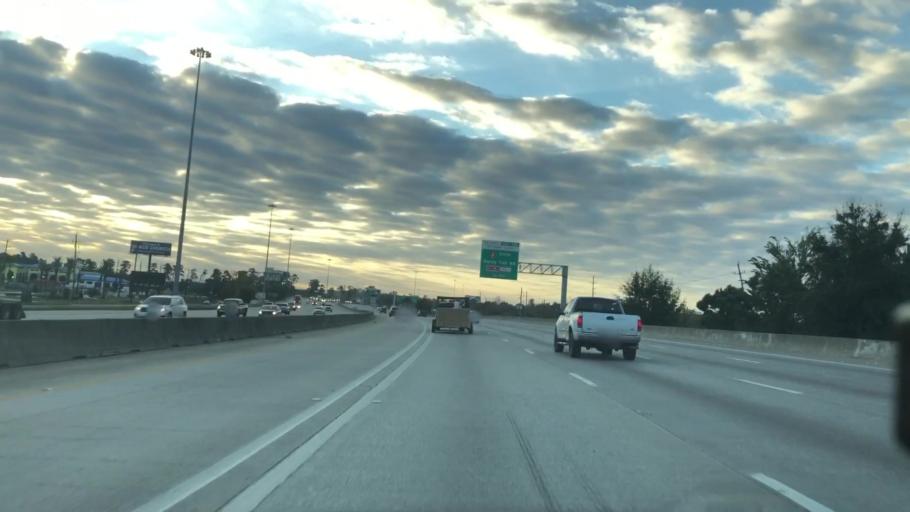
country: US
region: Texas
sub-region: Montgomery County
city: Oak Ridge North
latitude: 30.1184
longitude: -95.4411
